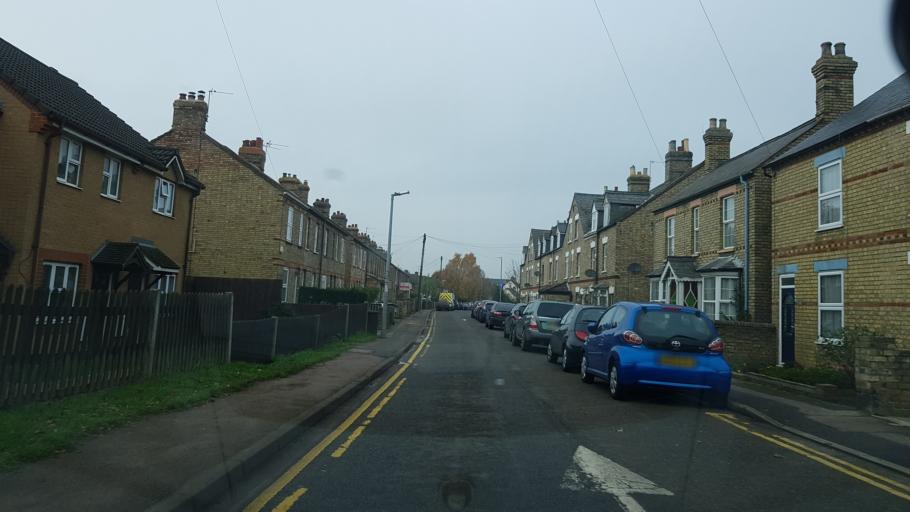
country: GB
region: England
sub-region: Central Bedfordshire
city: Biggleswade
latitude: 52.0897
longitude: -0.2632
